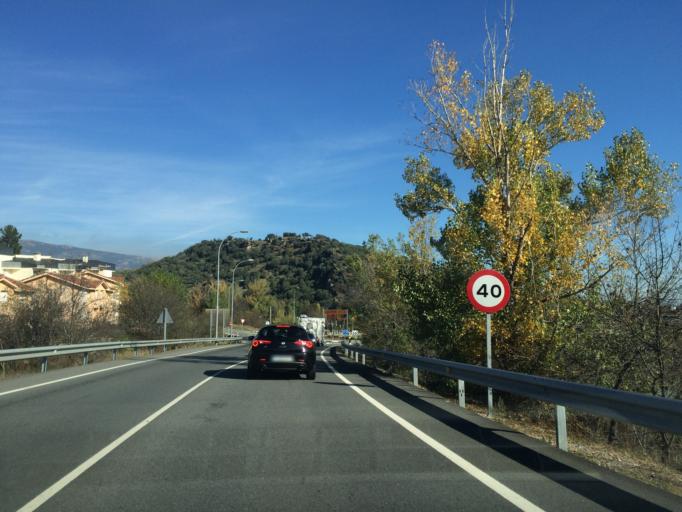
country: ES
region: Madrid
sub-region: Provincia de Madrid
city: Guadalix de la Sierra
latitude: 40.7865
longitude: -3.7071
